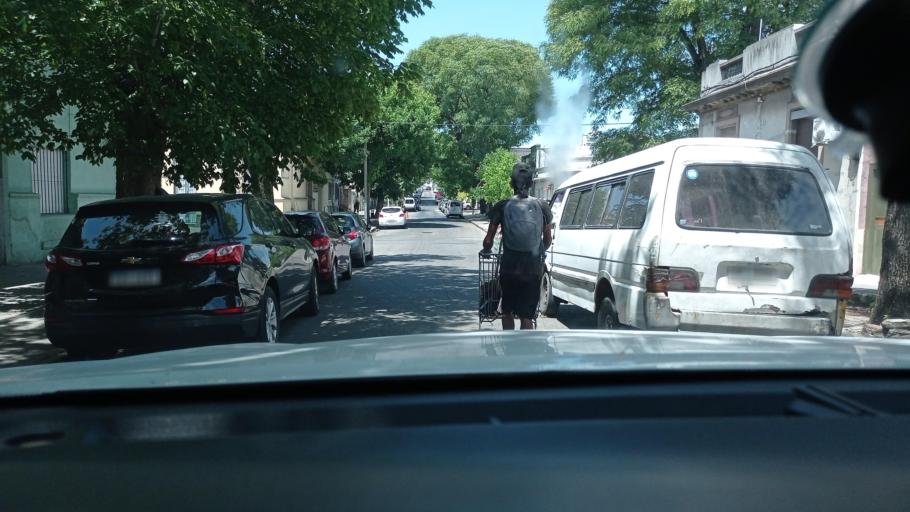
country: UY
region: Montevideo
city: Montevideo
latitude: -34.8872
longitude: -56.1686
